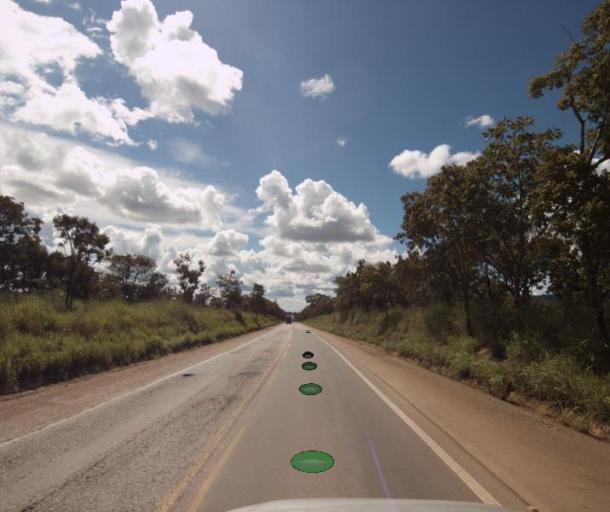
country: BR
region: Goias
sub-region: Porangatu
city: Porangatu
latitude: -13.6791
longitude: -49.0241
